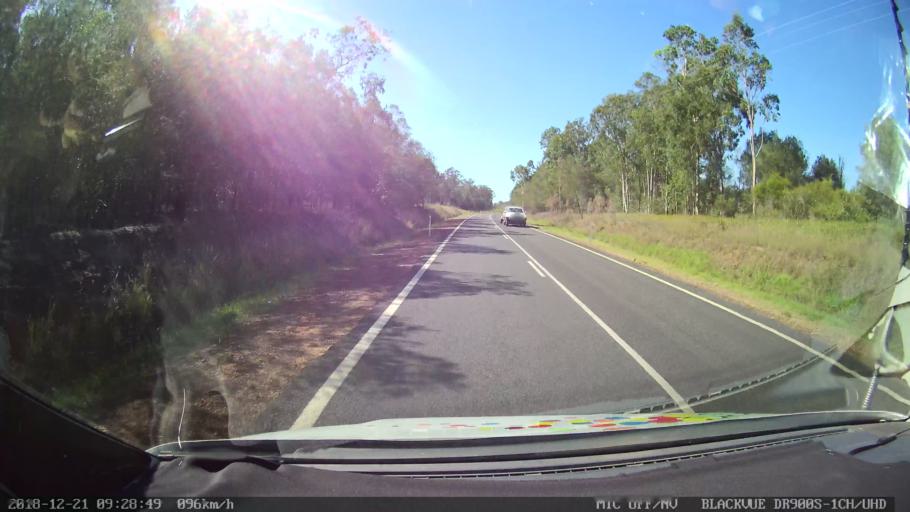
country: AU
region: New South Wales
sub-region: Clarence Valley
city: Maclean
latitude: -29.4227
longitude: 152.9883
